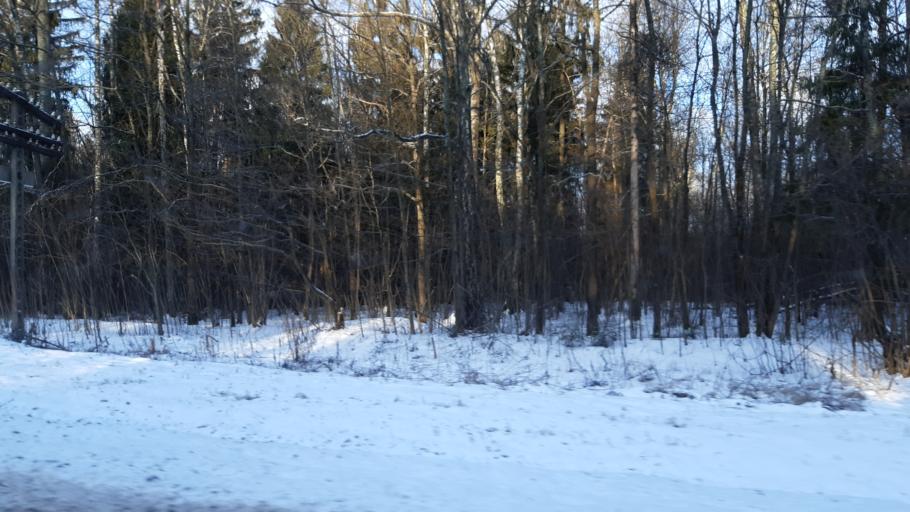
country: RU
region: Moskovskaya
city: Svatkovo
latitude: 56.3017
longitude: 38.3461
